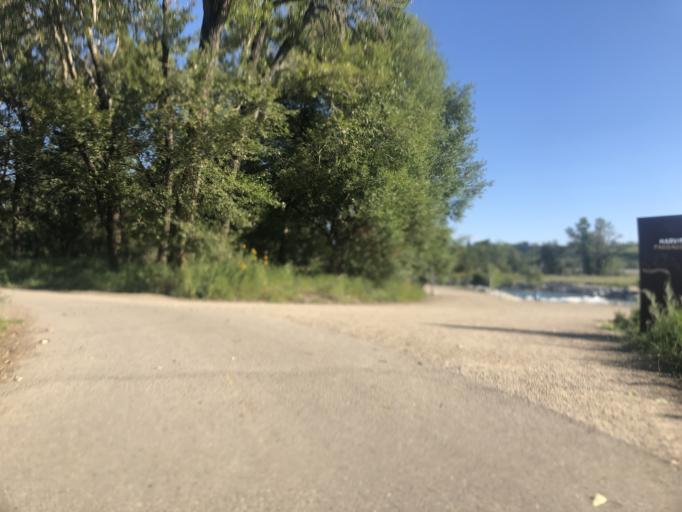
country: CA
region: Alberta
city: Calgary
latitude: 51.0398
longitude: -114.0123
